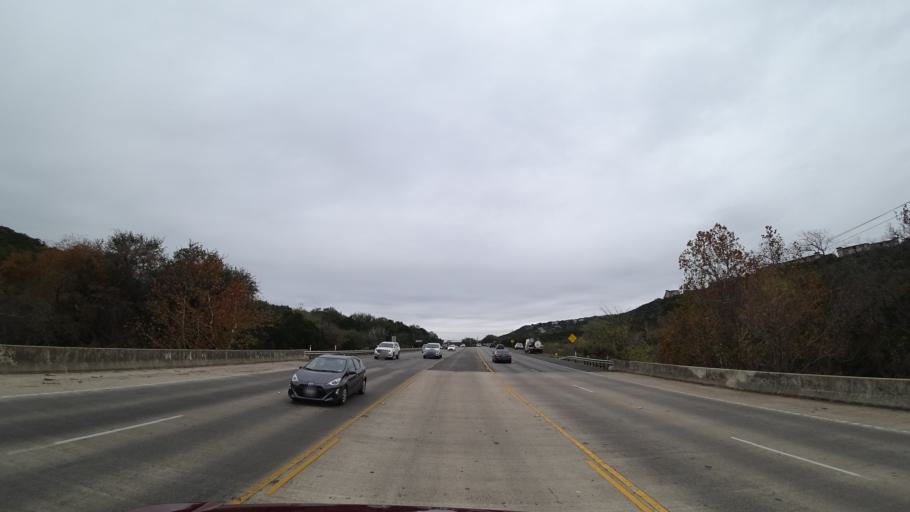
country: US
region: Texas
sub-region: Travis County
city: West Lake Hills
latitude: 30.3632
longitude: -97.7958
